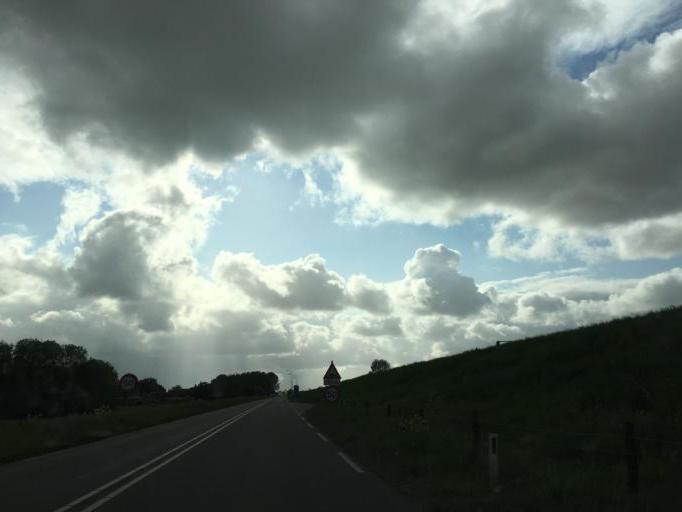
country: NL
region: North Holland
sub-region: Gemeente Medemblik
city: Opperdoes
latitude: 52.7511
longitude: 5.0203
